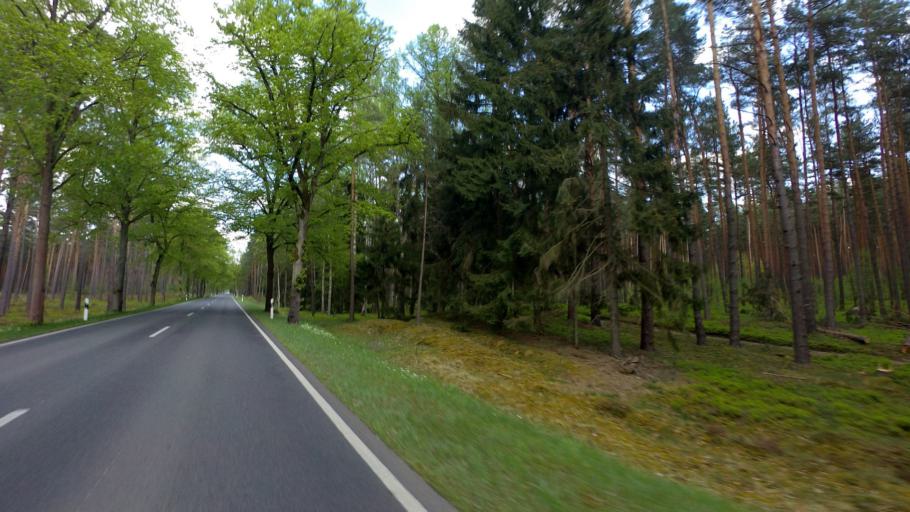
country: DE
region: Brandenburg
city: Marienwerder
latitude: 52.9477
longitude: 13.5608
